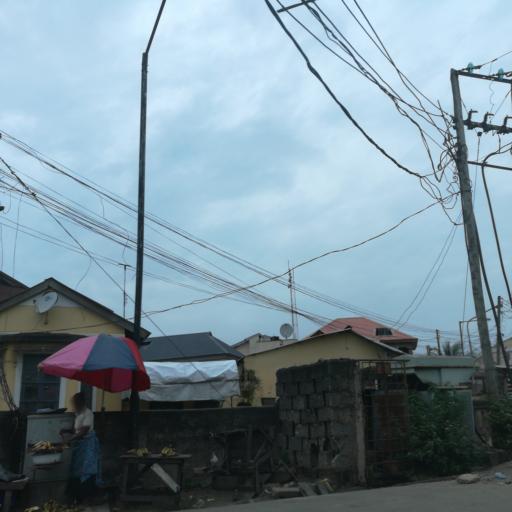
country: NG
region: Lagos
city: Makoko
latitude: 6.5031
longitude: 3.3784
